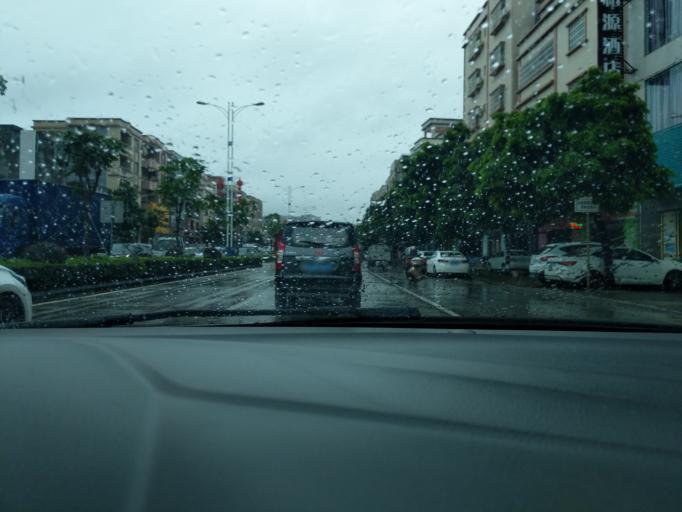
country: CN
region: Guangdong
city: Pingshi
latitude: 22.1975
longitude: 112.3330
